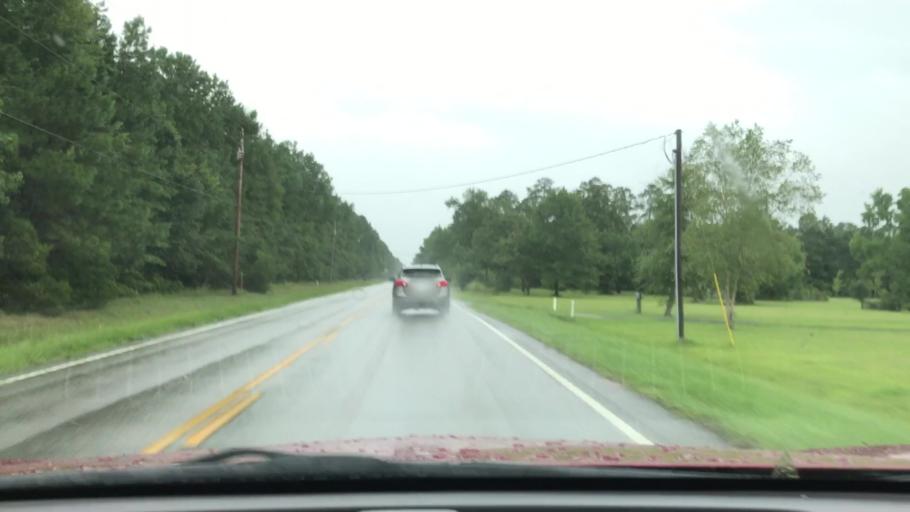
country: US
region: South Carolina
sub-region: Horry County
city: Conway
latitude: 33.7714
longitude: -79.0722
